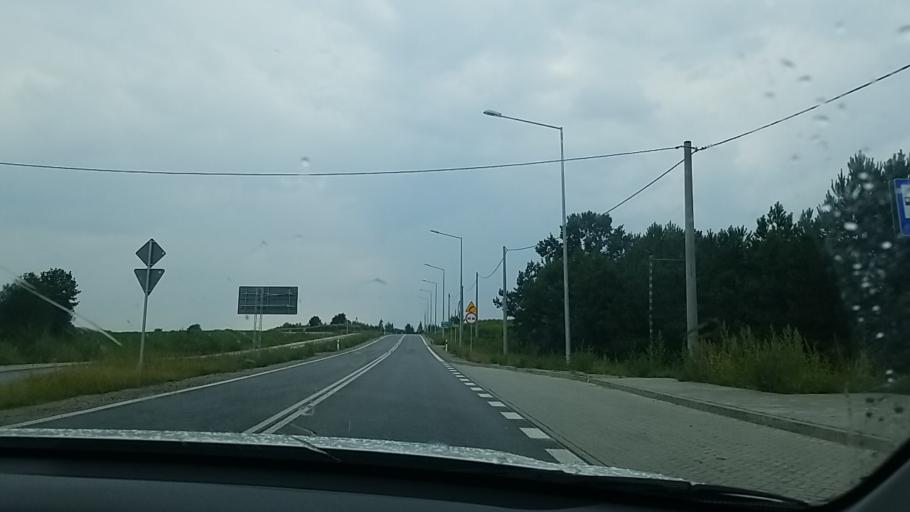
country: PL
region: Lublin Voivodeship
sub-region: Powiat lubelski
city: Krzczonow
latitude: 51.0004
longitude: 22.6770
